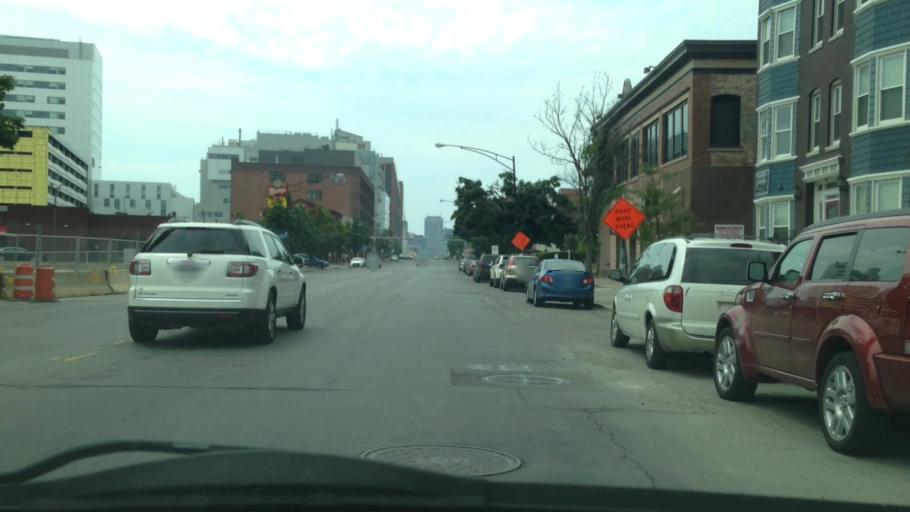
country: US
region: New York
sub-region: Erie County
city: Buffalo
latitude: 42.9040
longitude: -78.8685
